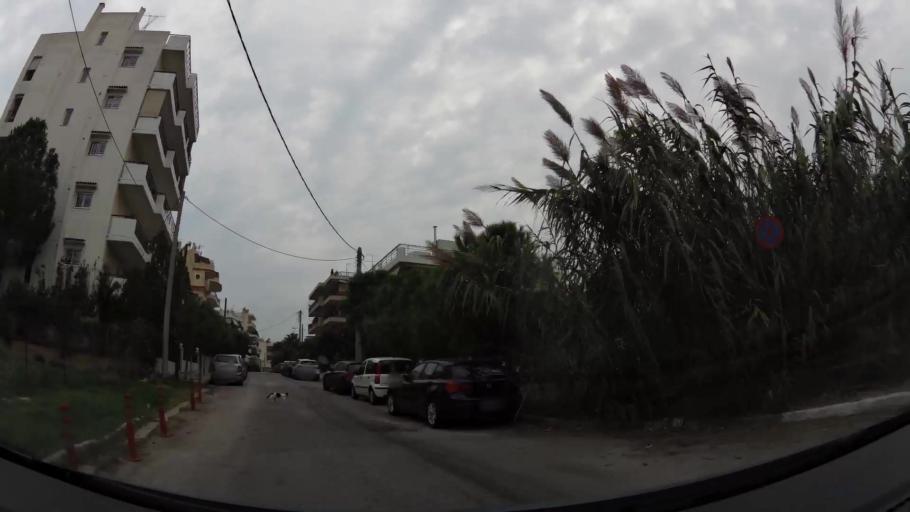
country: GR
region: Attica
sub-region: Nomarchia Athinas
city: Alimos
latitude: 37.9147
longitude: 23.7252
